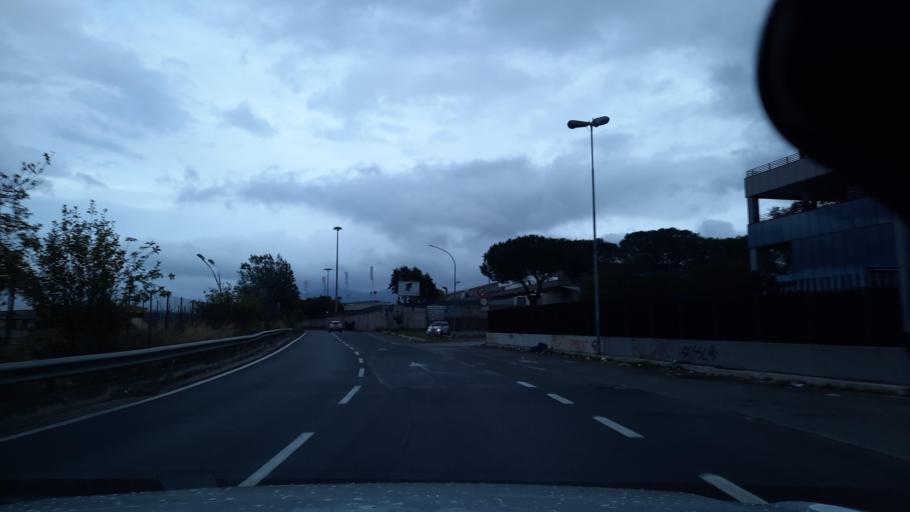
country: IT
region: Latium
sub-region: Citta metropolitana di Roma Capitale
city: Ciampino
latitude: 41.8493
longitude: 12.6063
